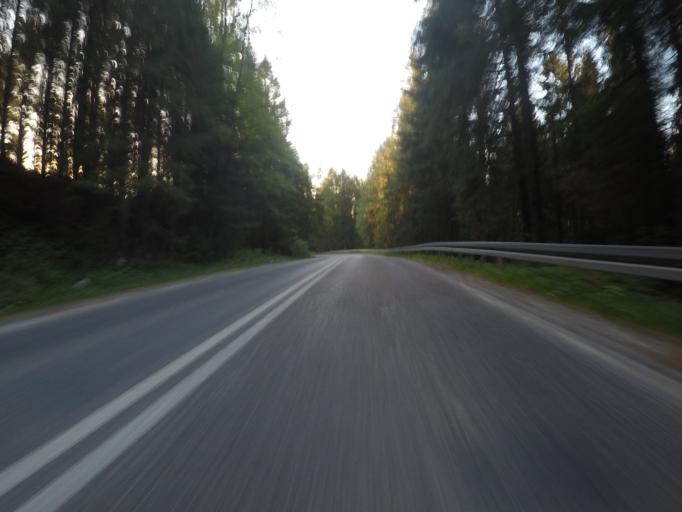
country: PL
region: Lesser Poland Voivodeship
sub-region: Powiat tatrzanski
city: Bukowina Tatrzanska
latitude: 49.2894
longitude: 20.0809
